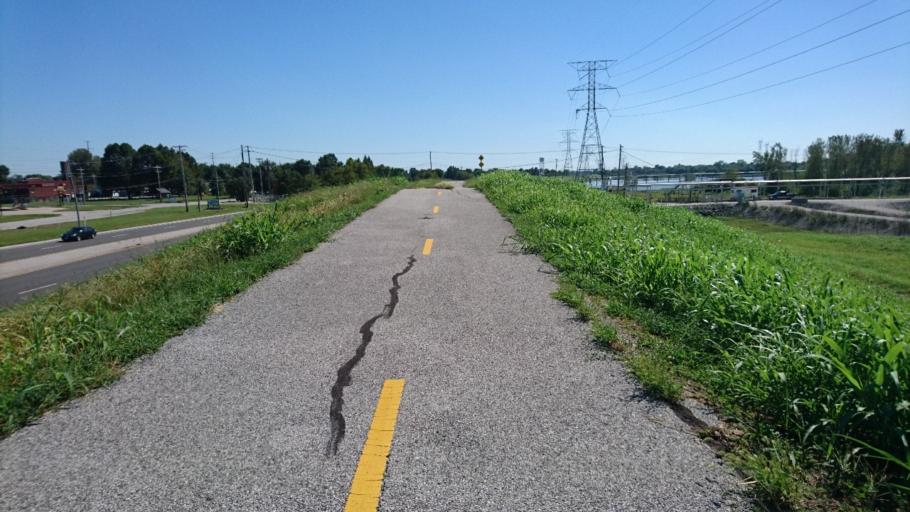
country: US
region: Illinois
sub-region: Madison County
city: Hartford
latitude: 38.8425
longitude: -90.0982
